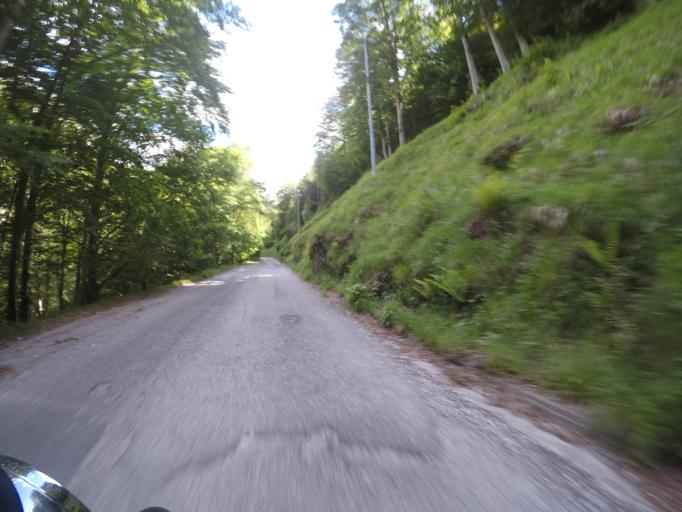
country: IT
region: Tuscany
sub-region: Provincia di Lucca
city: Minucciano
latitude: 44.1417
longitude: 10.1943
